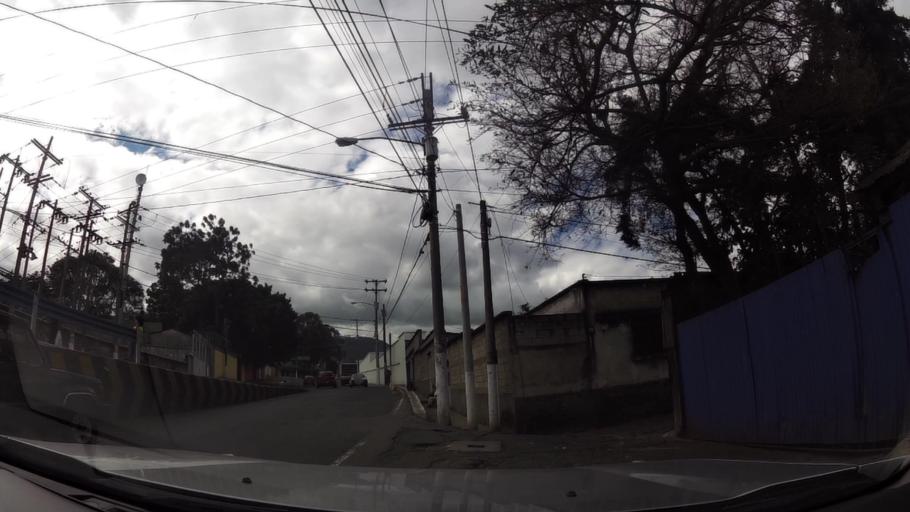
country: GT
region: Guatemala
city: Mixco
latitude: 14.6291
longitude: -90.6007
